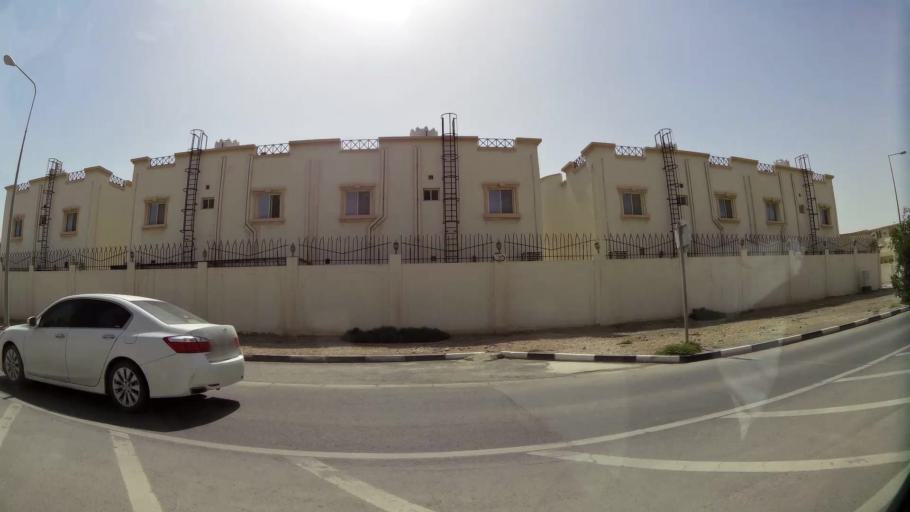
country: QA
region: Baladiyat Umm Salal
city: Umm Salal Muhammad
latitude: 25.3855
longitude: 51.4337
